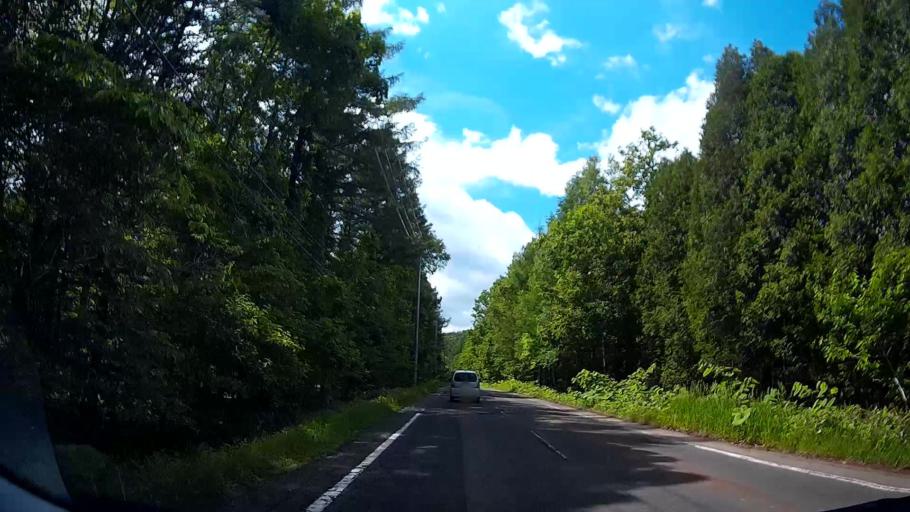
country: JP
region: Hokkaido
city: Kitahiroshima
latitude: 42.8429
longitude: 141.4761
